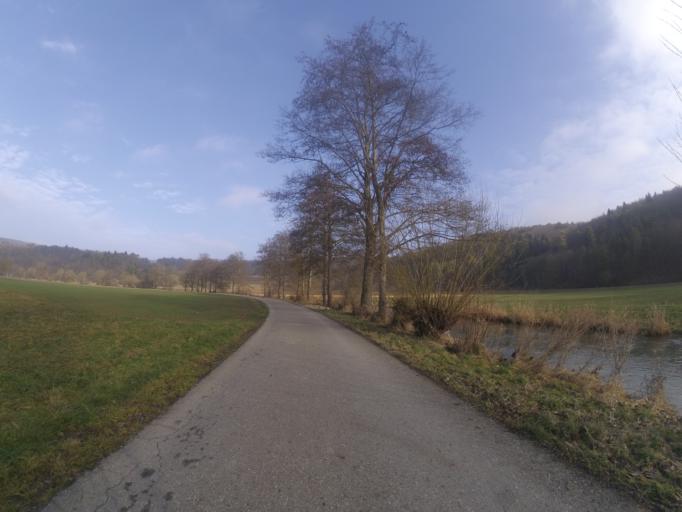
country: DE
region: Baden-Wuerttemberg
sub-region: Tuebingen Region
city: Rechtenstein
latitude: 48.2659
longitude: 9.5420
